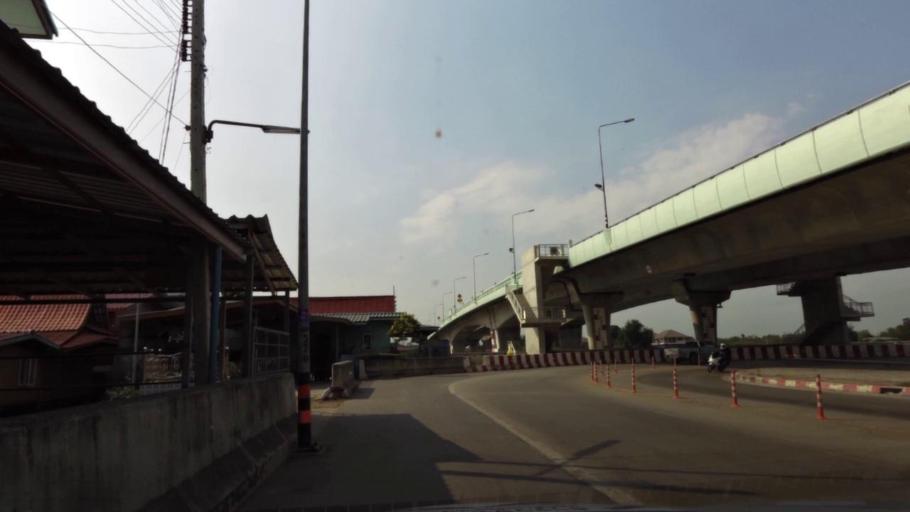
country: TH
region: Phra Nakhon Si Ayutthaya
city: Phra Nakhon Si Ayutthaya
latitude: 14.3277
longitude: 100.5785
